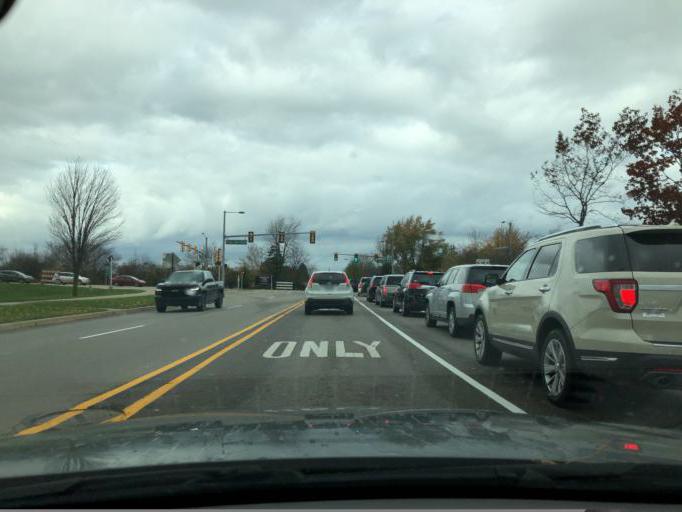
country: US
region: Michigan
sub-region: Washtenaw County
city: Ann Arbor
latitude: 42.2471
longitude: -83.7599
